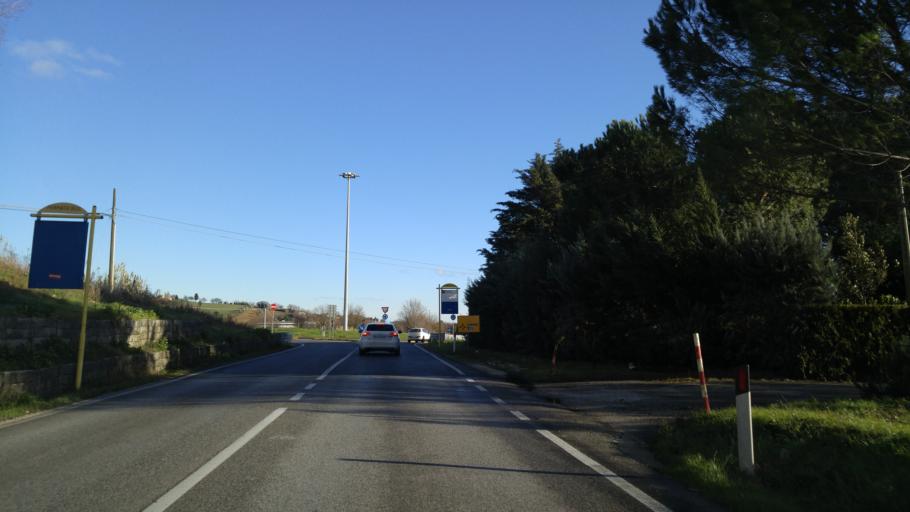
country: IT
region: The Marches
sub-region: Provincia di Ancona
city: Camerano
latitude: 43.5075
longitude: 13.5458
